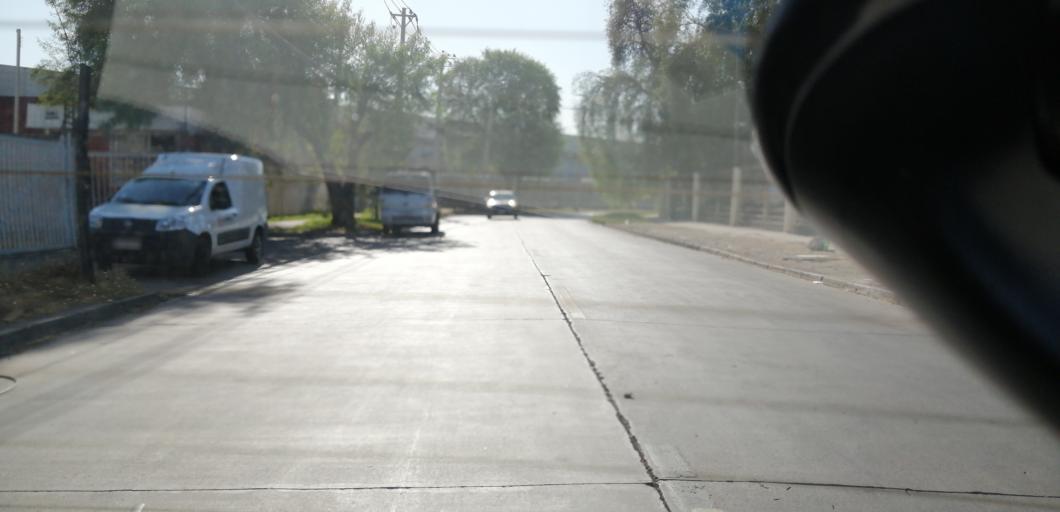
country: CL
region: Santiago Metropolitan
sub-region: Provincia de Santiago
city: Lo Prado
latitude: -33.3759
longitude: -70.7581
